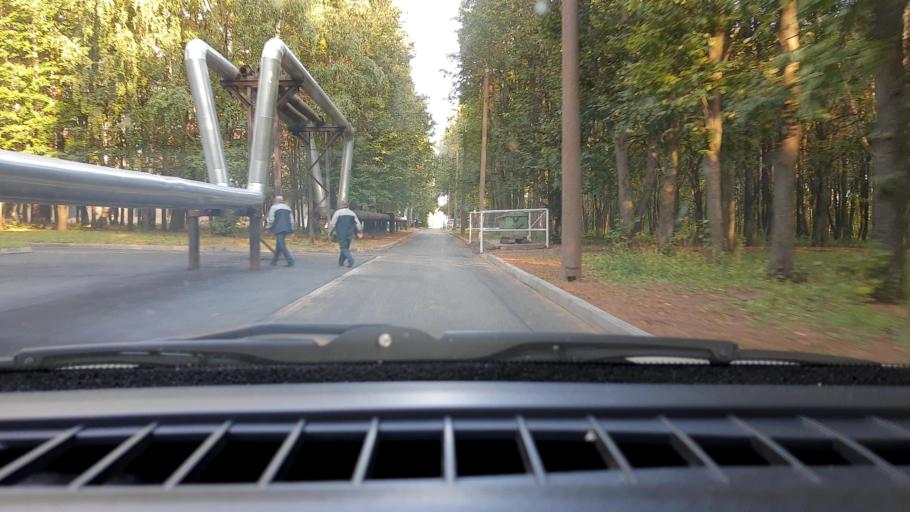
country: RU
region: Nizjnij Novgorod
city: Bor
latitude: 56.3105
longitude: 44.0811
